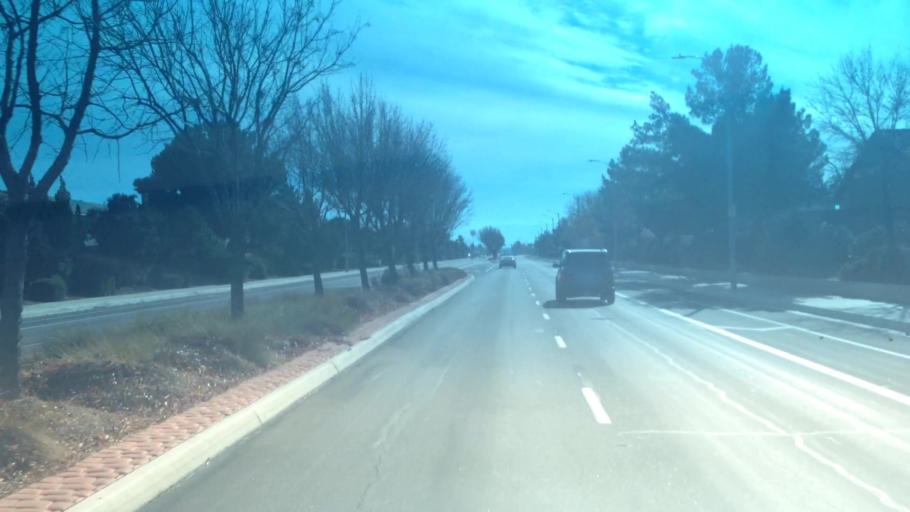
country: US
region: California
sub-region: Los Angeles County
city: Lancaster
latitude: 34.7095
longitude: -118.1661
